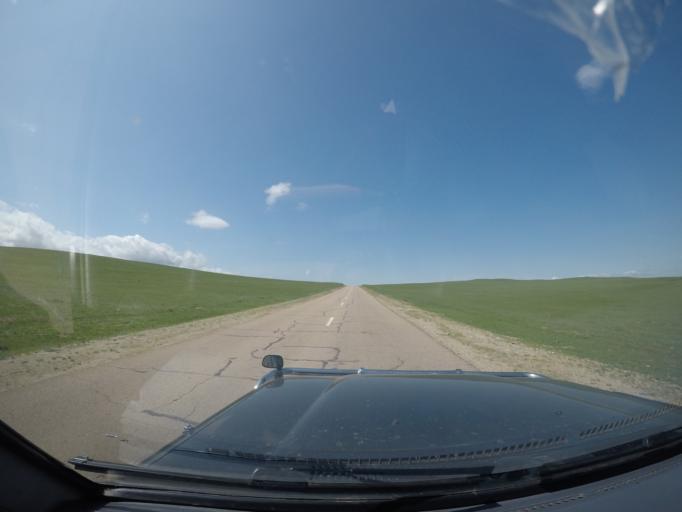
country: MN
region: Hentiy
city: Bayan
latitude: 47.2857
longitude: 110.9859
